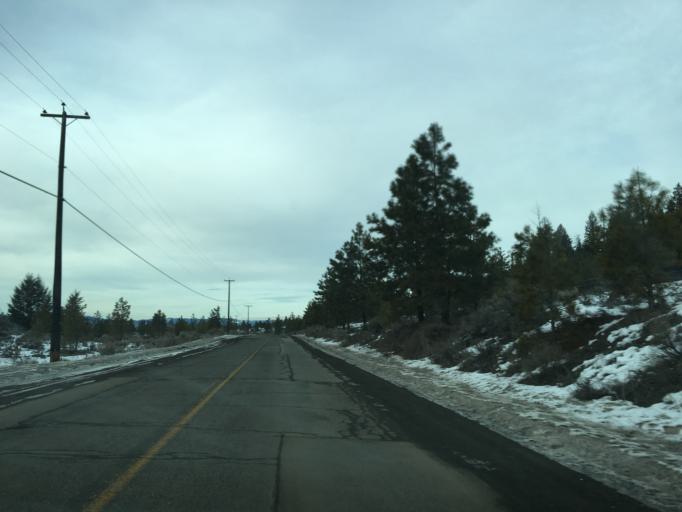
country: CA
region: British Columbia
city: Kamloops
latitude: 50.6440
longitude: -120.4500
